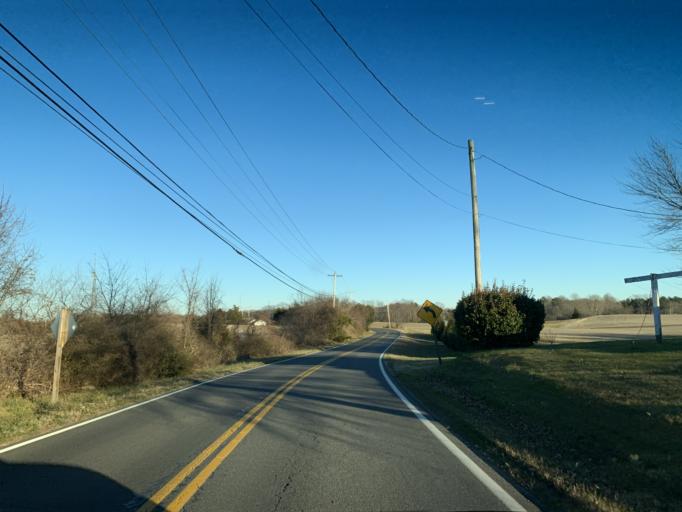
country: US
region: Maryland
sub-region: Saint Mary's County
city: Mechanicsville
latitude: 38.4421
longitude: -76.7344
